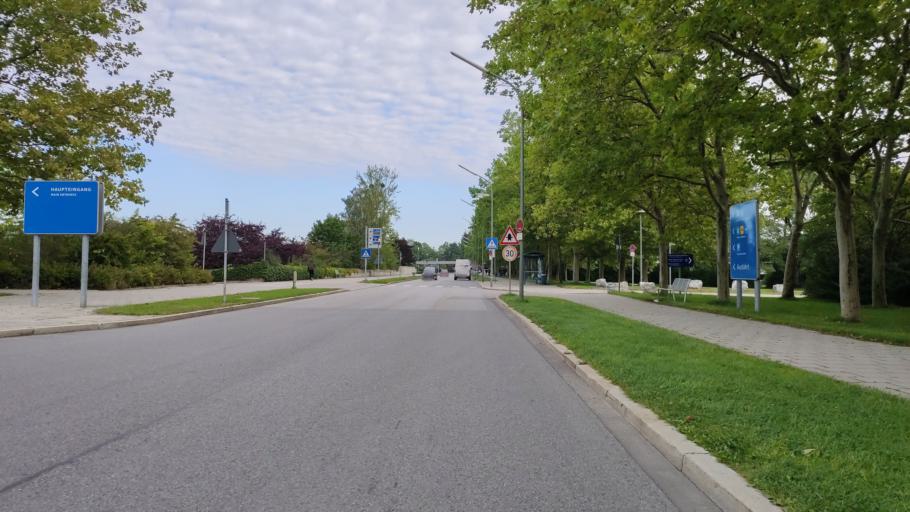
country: DE
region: Bavaria
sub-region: Upper Bavaria
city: Neuried
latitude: 48.1111
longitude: 11.4740
